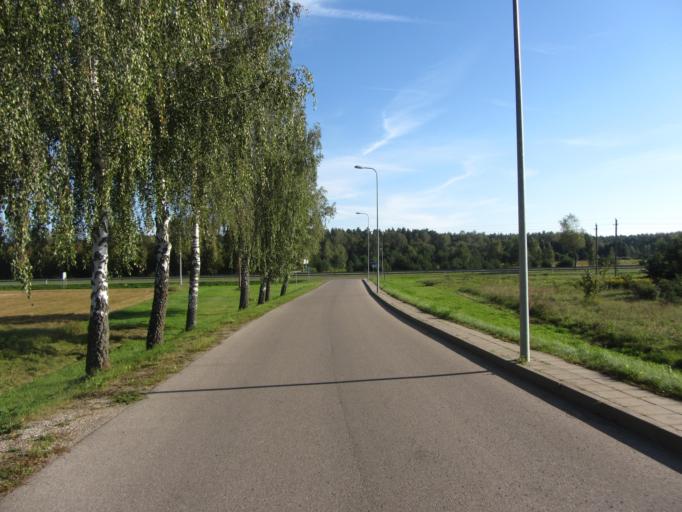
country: LT
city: Birstonas
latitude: 54.6092
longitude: 24.0010
